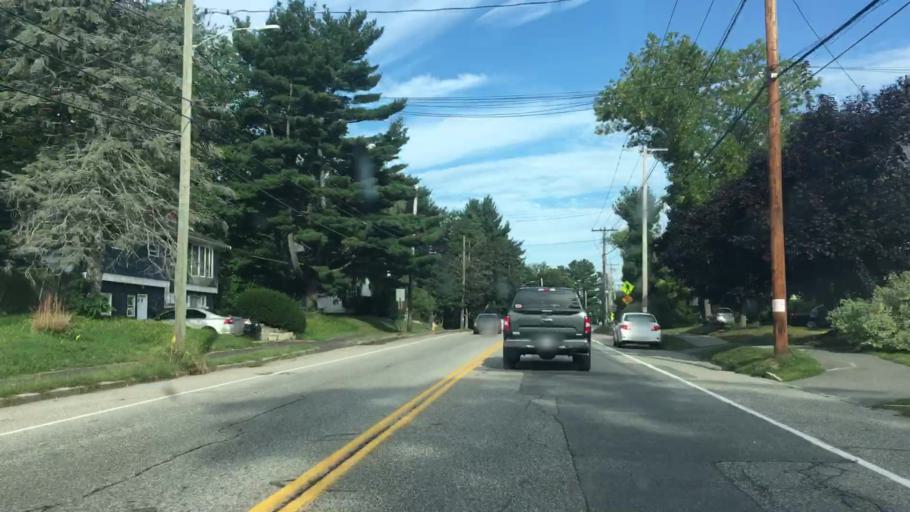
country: US
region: Maine
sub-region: Cumberland County
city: Portland
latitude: 43.6918
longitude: -70.2801
